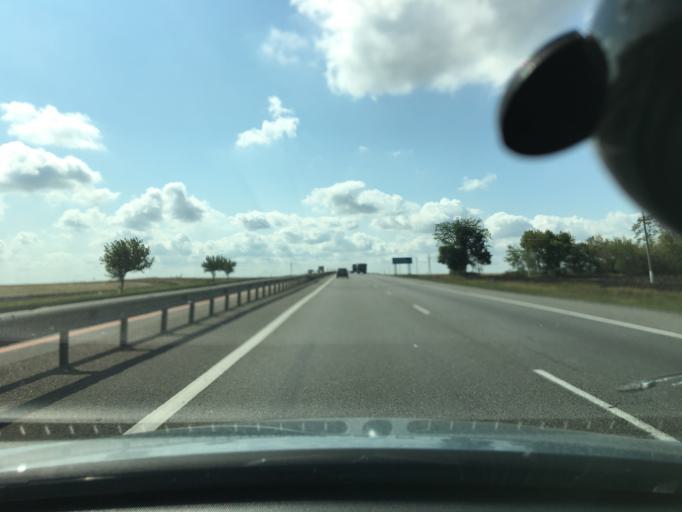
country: RU
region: Krasnodarskiy
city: Krasnoye
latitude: 46.7269
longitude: 39.6555
